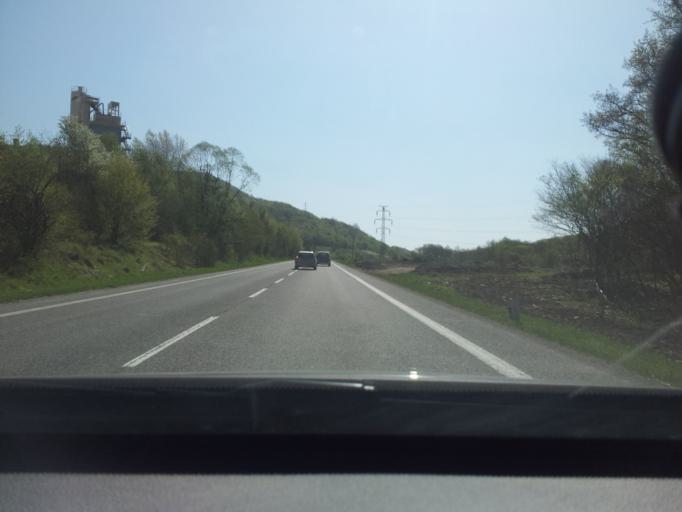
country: SK
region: Trenciansky
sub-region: Okres Trencin
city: Trencin
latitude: 48.8250
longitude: 18.0688
